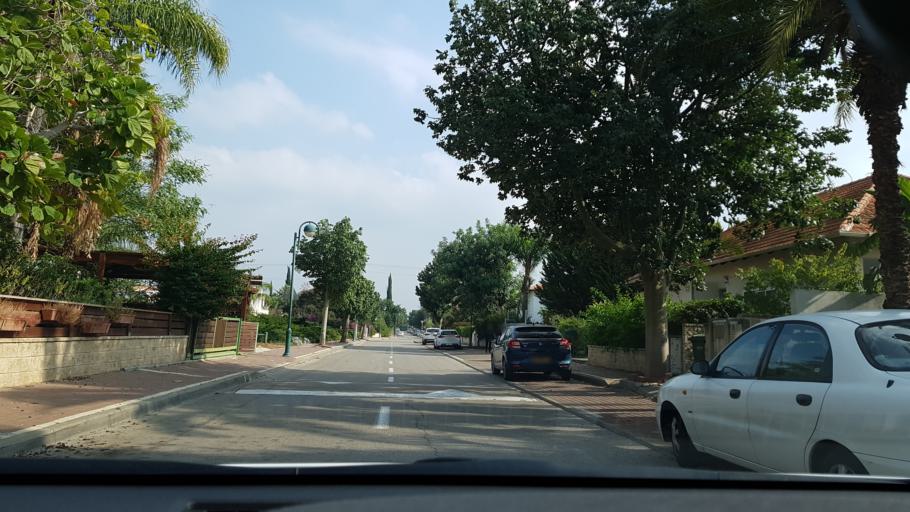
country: IL
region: Central District
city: Mazkeret Batya
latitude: 31.8730
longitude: 34.8263
